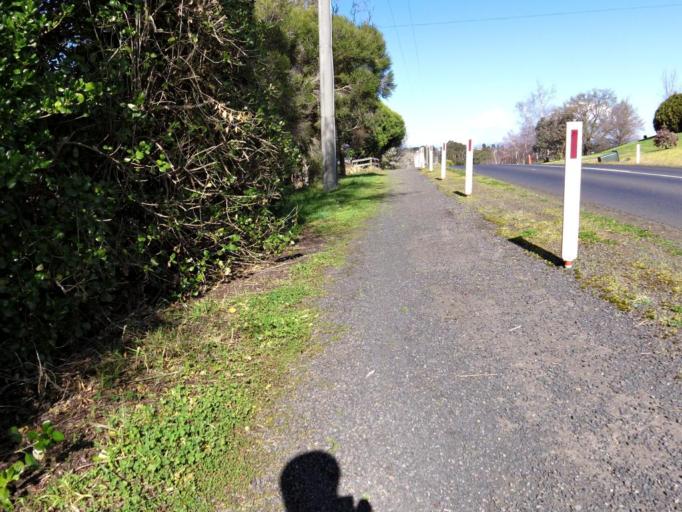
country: AU
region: Victoria
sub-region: Baw Baw
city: Warragul
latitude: -37.9989
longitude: 145.9521
